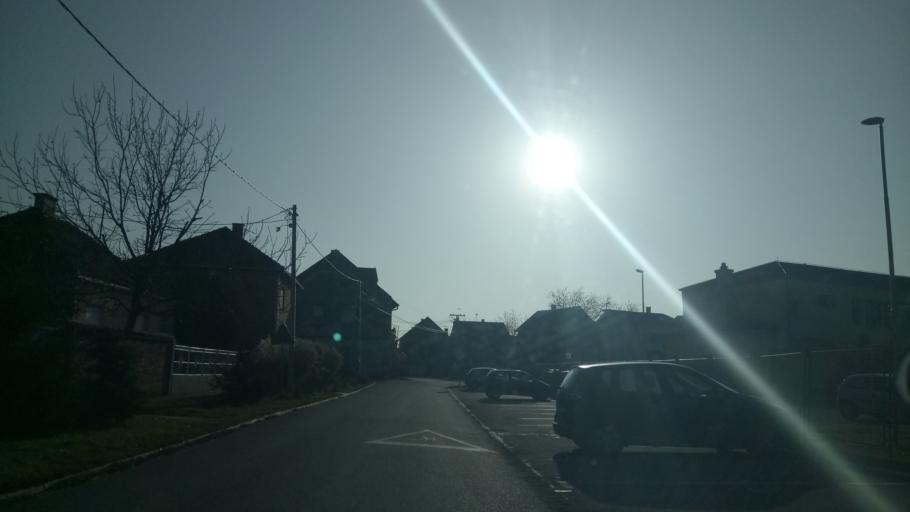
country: RS
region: Autonomna Pokrajina Vojvodina
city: Nova Pazova
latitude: 44.9437
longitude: 20.2140
